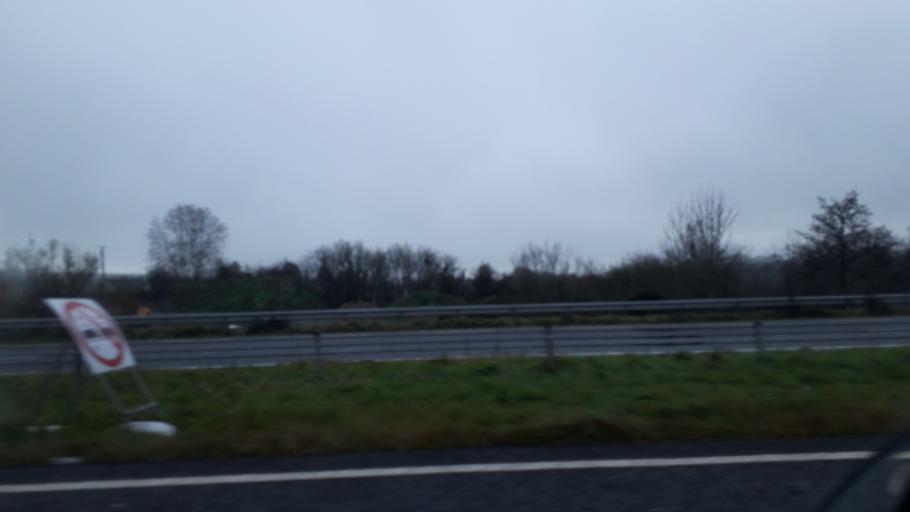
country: IE
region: Ulster
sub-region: County Donegal
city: Raphoe
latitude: 54.9465
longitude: -7.6456
